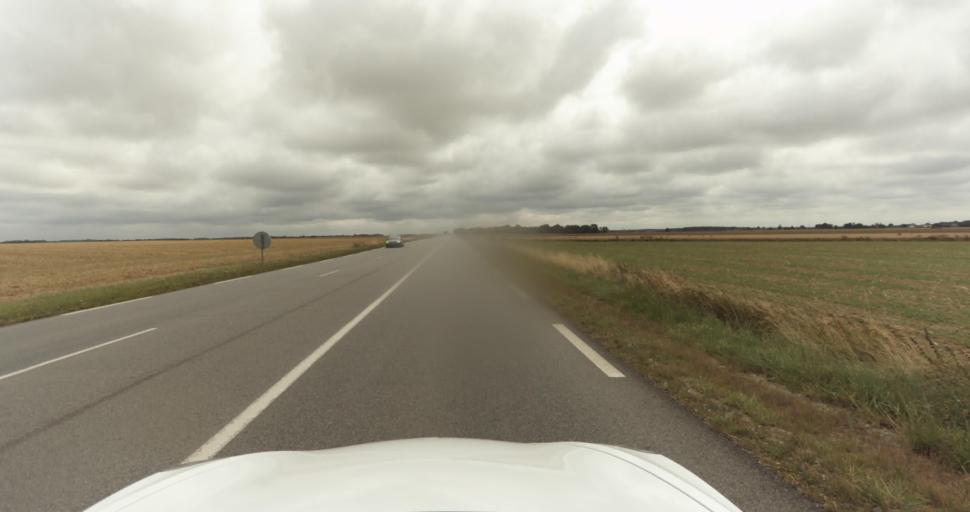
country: FR
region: Haute-Normandie
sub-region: Departement de l'Eure
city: Claville
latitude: 49.0590
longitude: 1.0423
